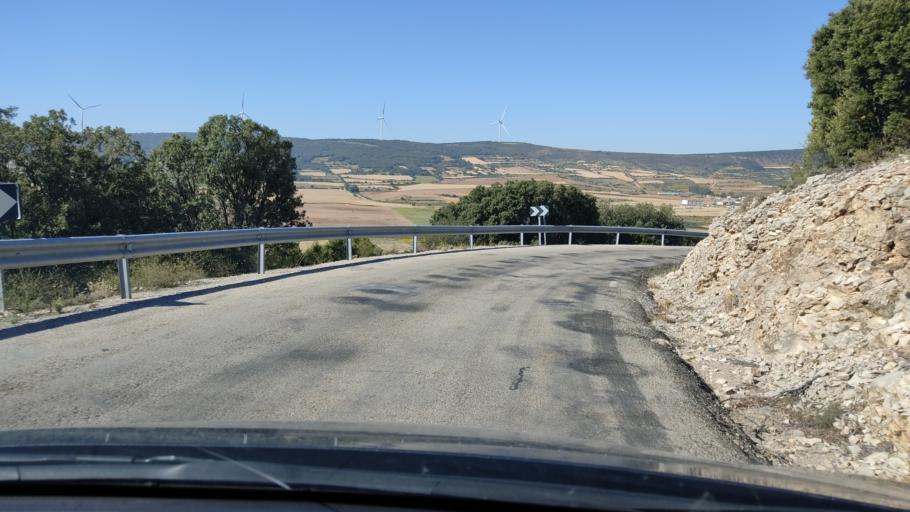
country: ES
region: Aragon
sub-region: Provincia de Teruel
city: Fonfria
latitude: 41.0026
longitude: -1.0675
